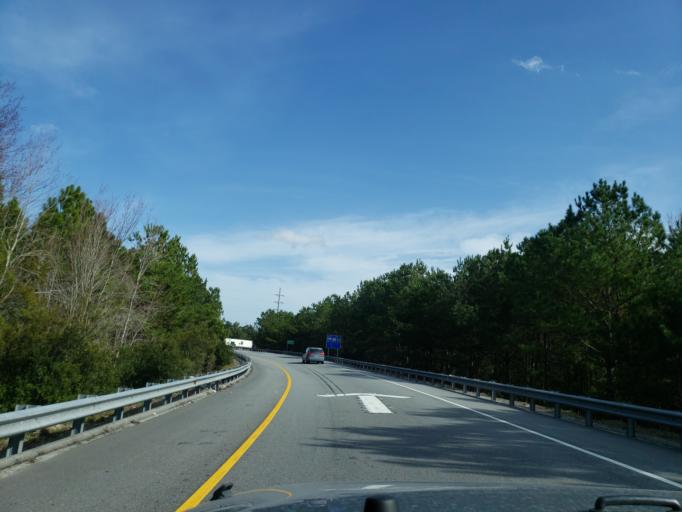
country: US
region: Georgia
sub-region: Chatham County
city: Port Wentworth
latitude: 32.1637
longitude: -81.2160
